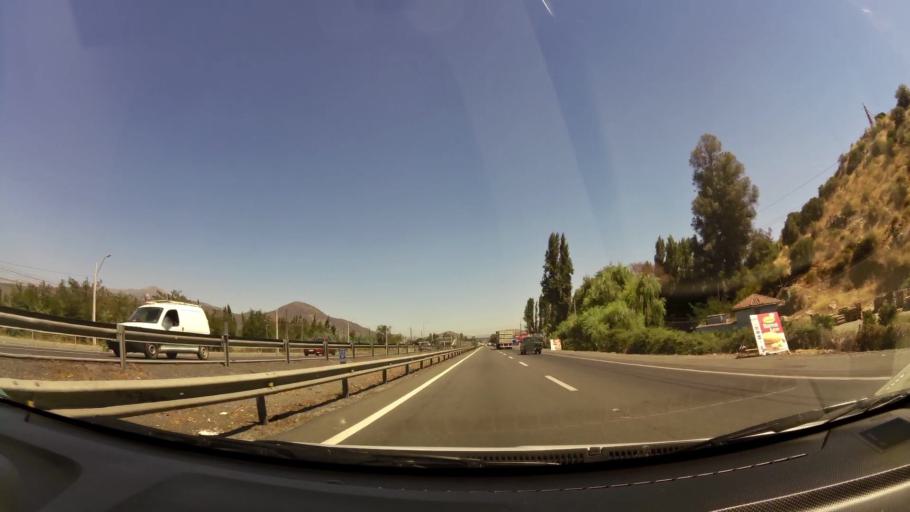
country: CL
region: O'Higgins
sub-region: Provincia de Cachapoal
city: Rengo
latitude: -34.4323
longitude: -70.8872
